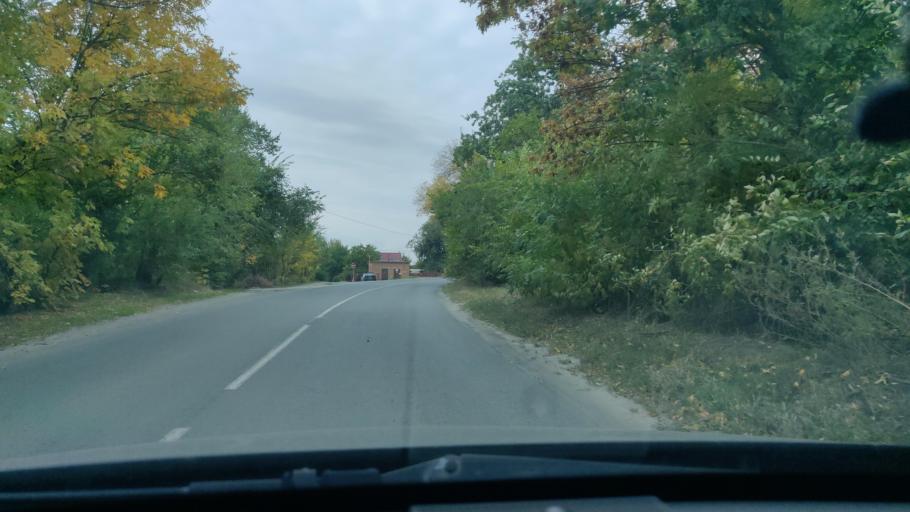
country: RU
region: Rostov
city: Ust'-Donetskiy
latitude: 47.6478
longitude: 40.8874
